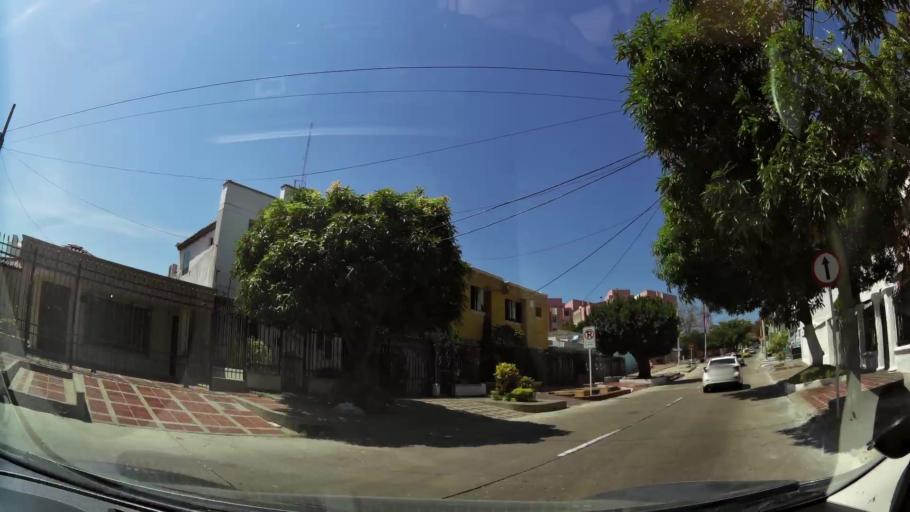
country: CO
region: Atlantico
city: Barranquilla
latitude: 10.9870
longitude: -74.8090
